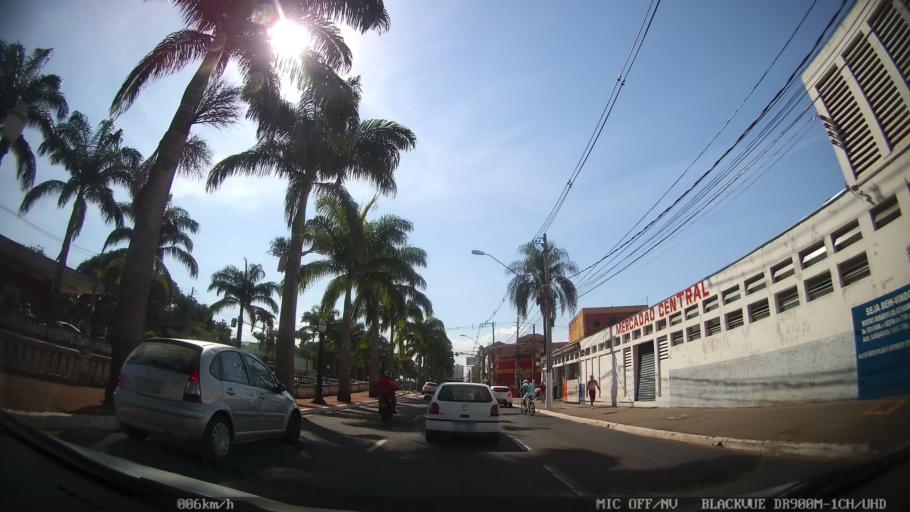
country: BR
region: Sao Paulo
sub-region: Ribeirao Preto
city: Ribeirao Preto
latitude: -21.1739
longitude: -47.8136
